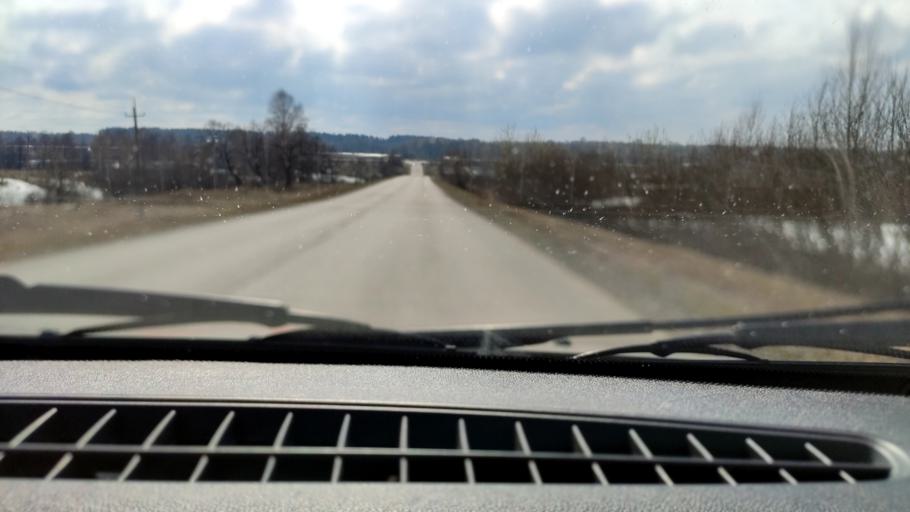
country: RU
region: Bashkortostan
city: Kudeyevskiy
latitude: 54.8224
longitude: 56.7933
